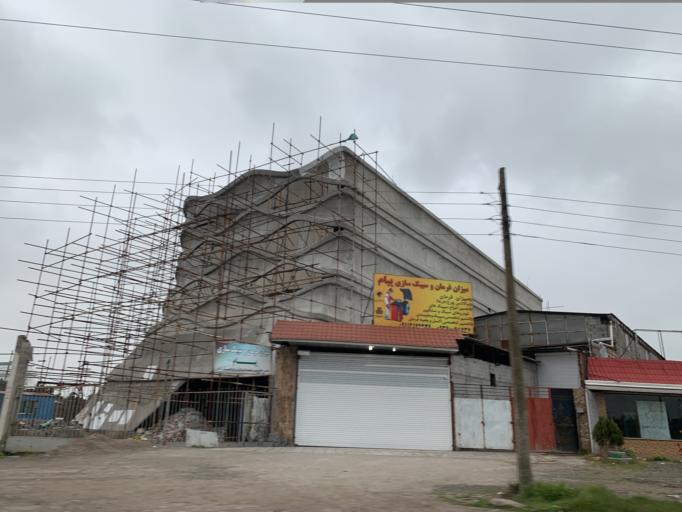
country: IR
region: Mazandaran
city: Babol
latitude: 36.5279
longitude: 52.6252
